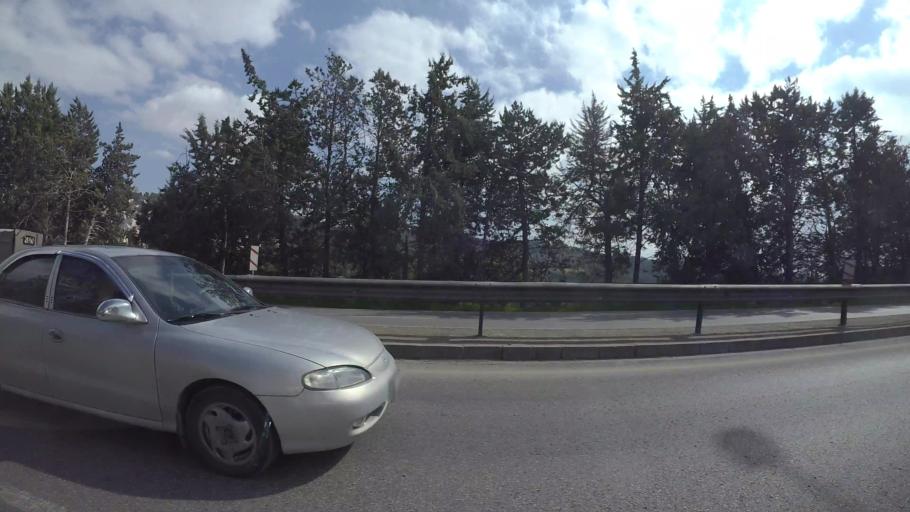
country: JO
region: Amman
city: Al Jubayhah
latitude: 32.0288
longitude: 35.8177
